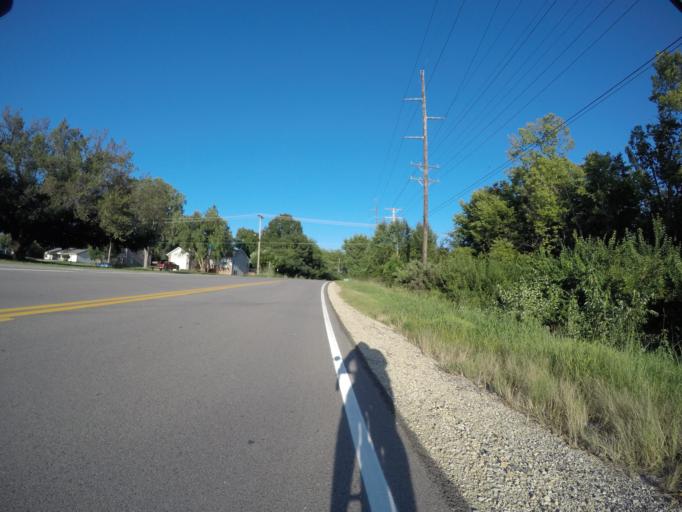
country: US
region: Kansas
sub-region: Riley County
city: Manhattan
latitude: 39.1600
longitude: -96.6117
